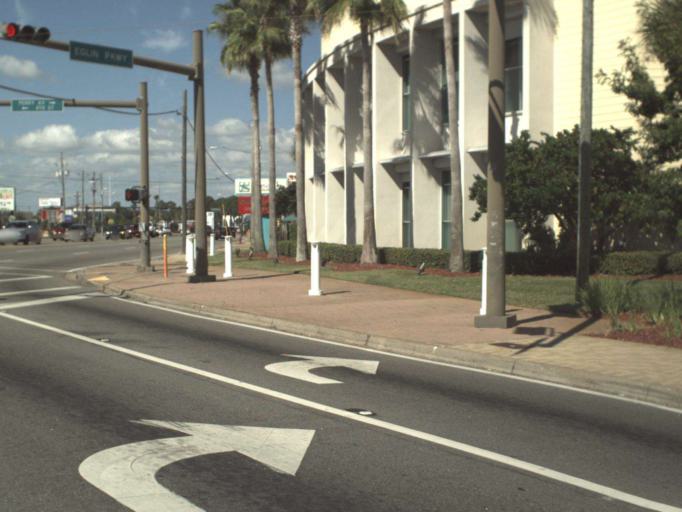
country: US
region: Florida
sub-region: Okaloosa County
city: Fort Walton Beach
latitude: 30.4102
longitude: -86.6036
